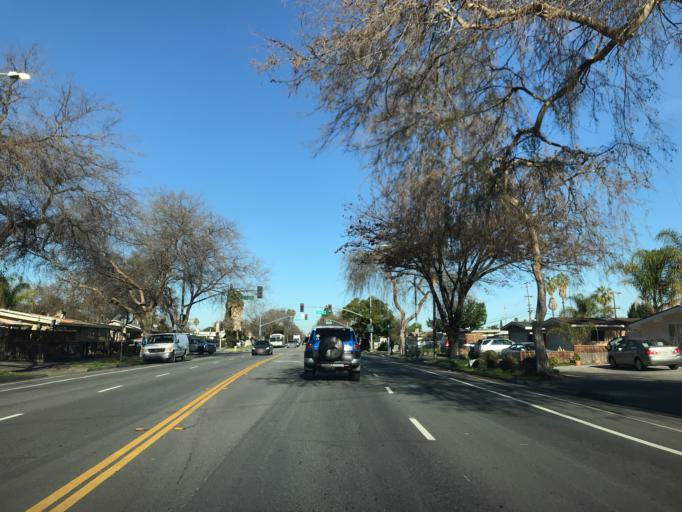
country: US
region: California
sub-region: Santa Clara County
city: Alum Rock
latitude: 37.3330
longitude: -121.8363
